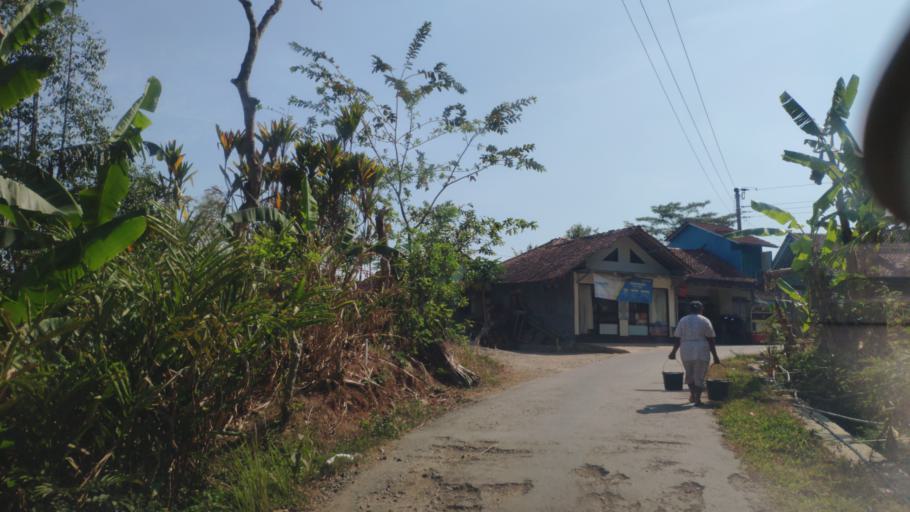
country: ID
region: Central Java
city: Gombong
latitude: -7.4550
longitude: 109.6415
